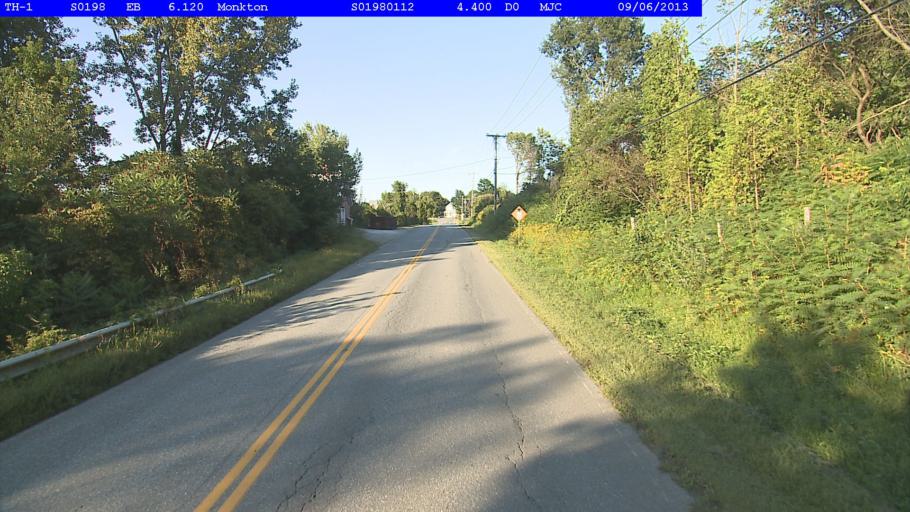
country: US
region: Vermont
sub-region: Chittenden County
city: Hinesburg
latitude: 44.2509
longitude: -73.1262
